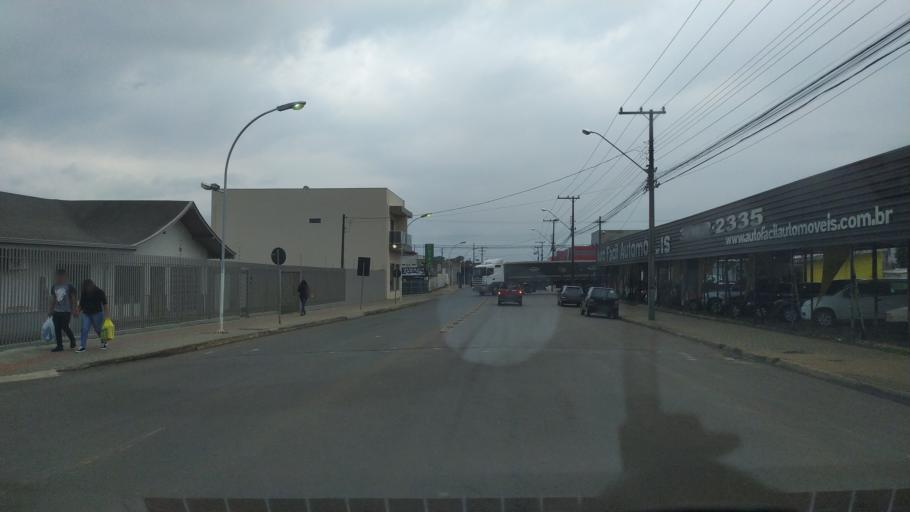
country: BR
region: Parana
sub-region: Palmas
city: Palmas
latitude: -26.4879
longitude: -51.9979
